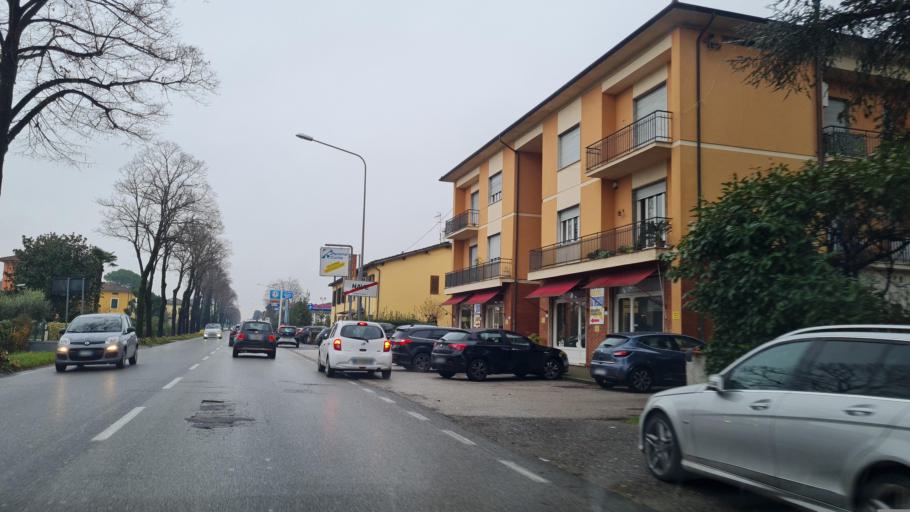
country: IT
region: Tuscany
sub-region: Provincia di Lucca
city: Lucca
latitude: 43.8490
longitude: 10.4648
